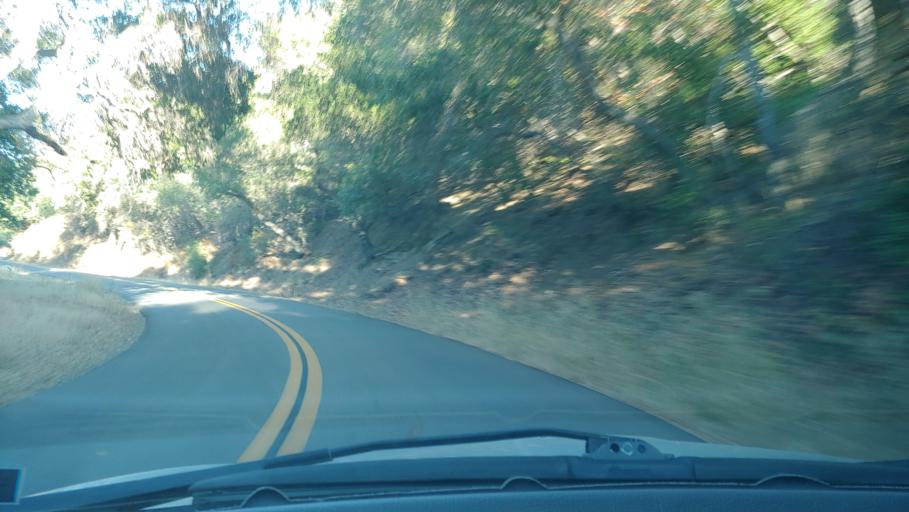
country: US
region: California
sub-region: Santa Barbara County
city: Goleta
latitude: 34.5350
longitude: -119.8506
